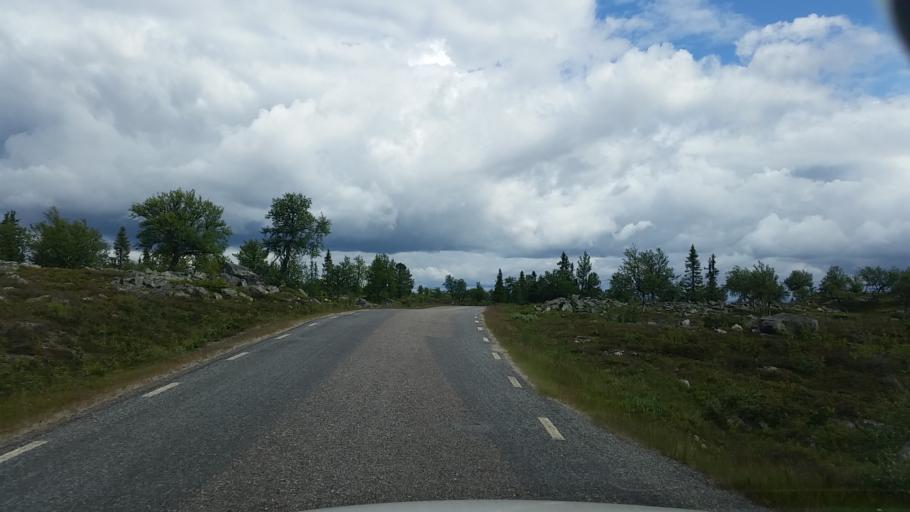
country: NO
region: Hedmark
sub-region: Trysil
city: Innbygda
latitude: 62.1370
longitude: 13.0328
